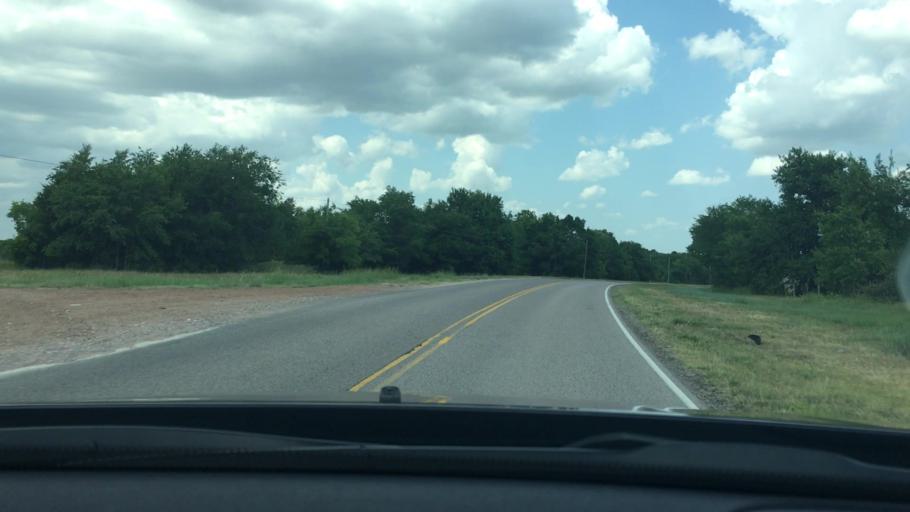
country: US
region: Oklahoma
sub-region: Johnston County
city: Tishomingo
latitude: 34.4717
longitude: -96.6357
